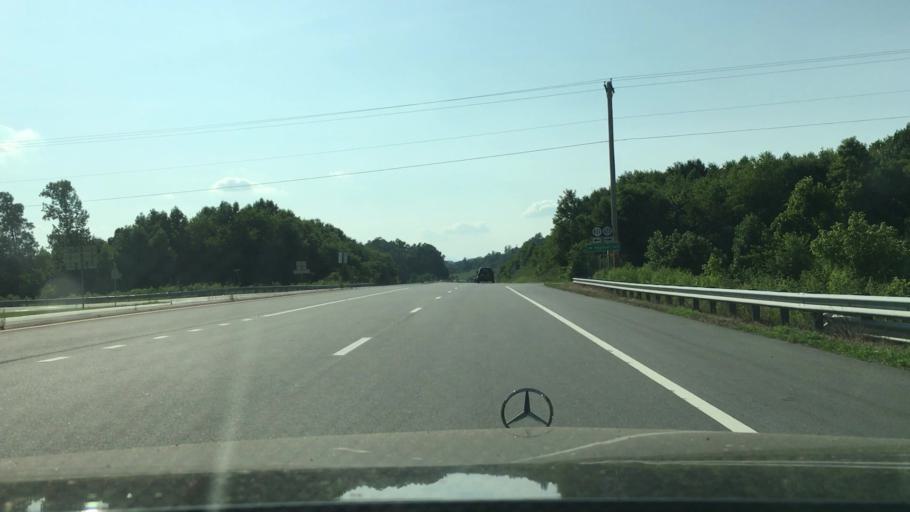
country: US
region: Virginia
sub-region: Amherst County
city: Madison Heights
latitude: 37.4095
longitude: -79.0880
